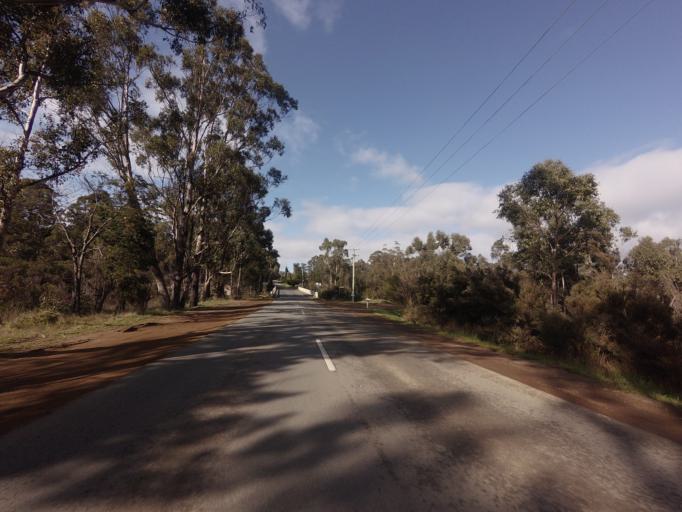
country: AU
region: Tasmania
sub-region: Huon Valley
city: Geeveston
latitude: -43.3302
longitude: 146.9707
